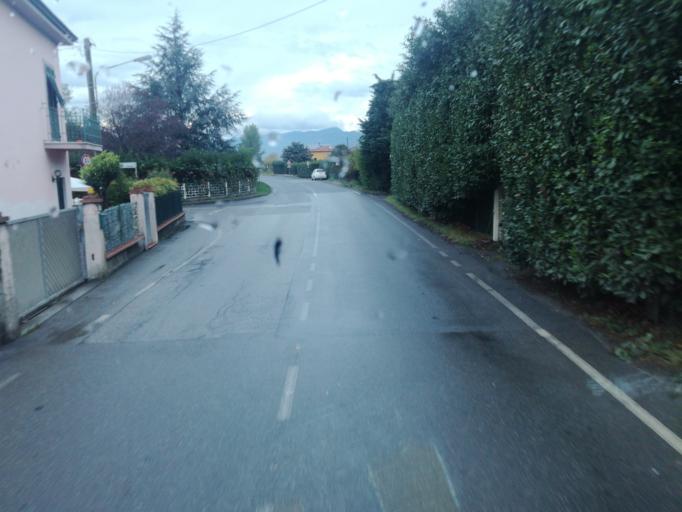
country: IT
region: Liguria
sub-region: Provincia di La Spezia
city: Arcola
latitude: 44.1238
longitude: 9.9153
